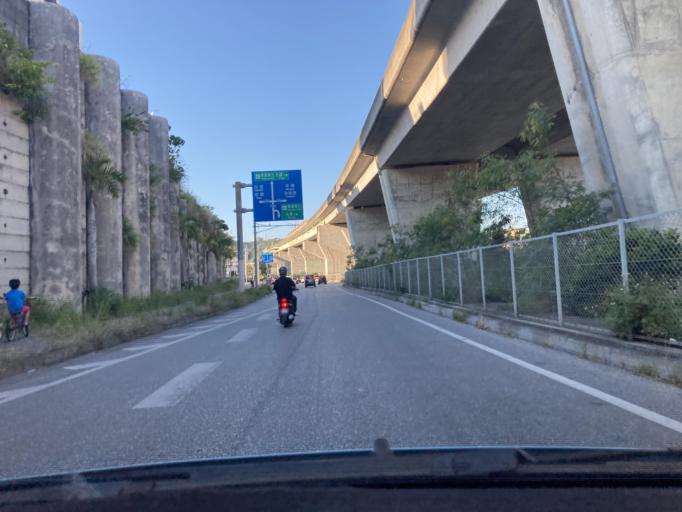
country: JP
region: Okinawa
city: Tomigusuku
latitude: 26.1987
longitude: 127.7397
